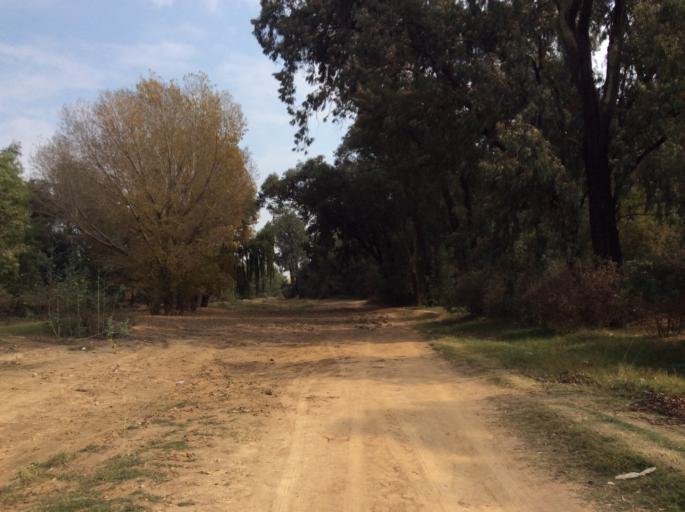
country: LS
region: Mafeteng
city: Mafeteng
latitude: -29.7259
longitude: 27.0305
